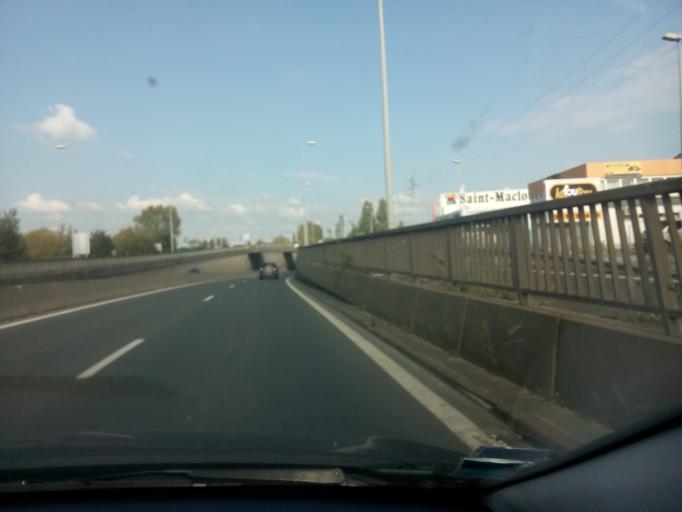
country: FR
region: Pays de la Loire
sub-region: Departement de Maine-et-Loire
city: Angers
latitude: 47.4874
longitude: -0.5467
